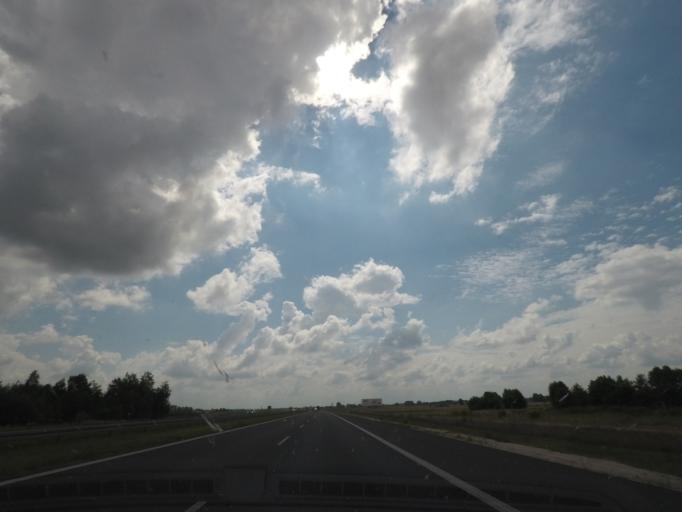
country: PL
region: Lodz Voivodeship
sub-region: Powiat zgierski
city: Strykow
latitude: 51.9884
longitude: 19.5538
